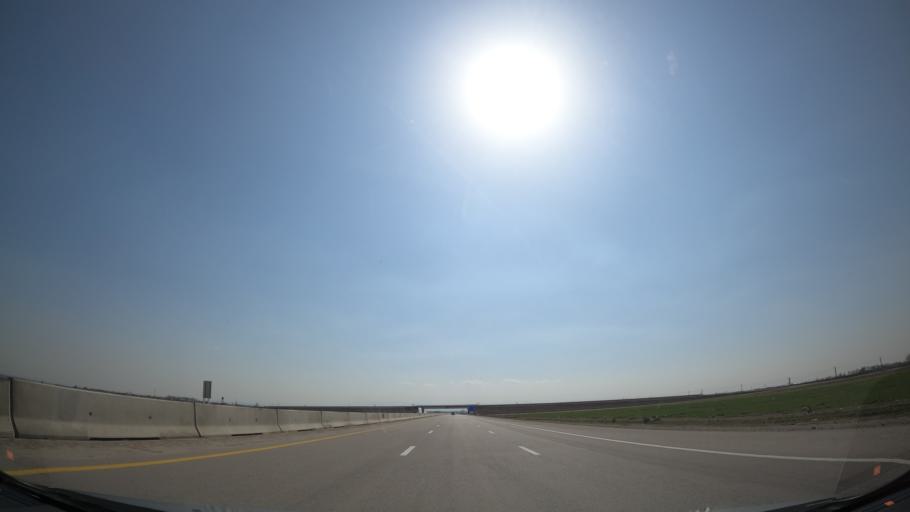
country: IR
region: Qazvin
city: Abyek
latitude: 36.0045
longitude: 50.4616
